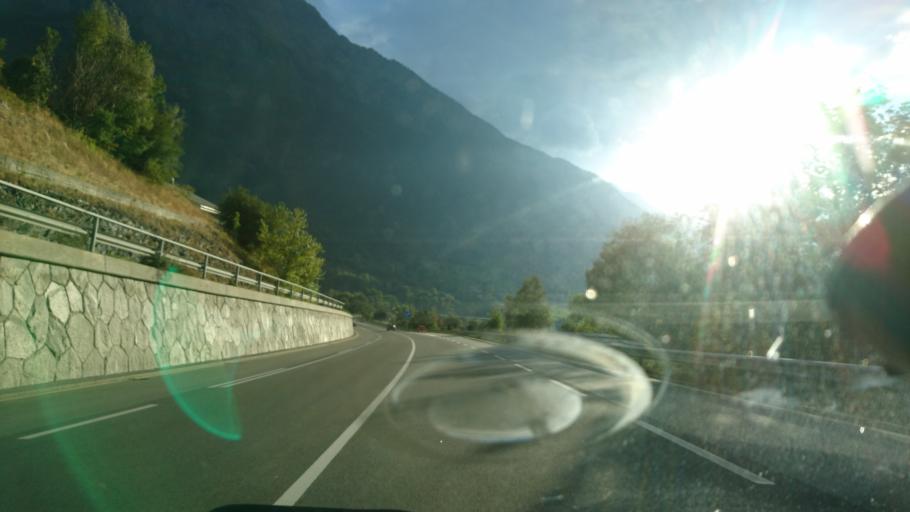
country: CH
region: Valais
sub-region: Brig District
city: Naters
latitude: 46.3136
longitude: 8.0025
